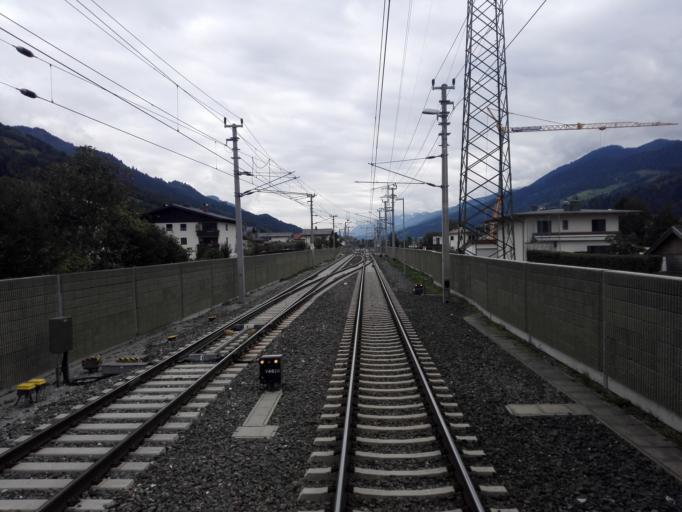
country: AT
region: Salzburg
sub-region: Politischer Bezirk Zell am See
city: Bruck an der Grossglocknerstrasse
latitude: 47.2844
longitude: 12.8212
